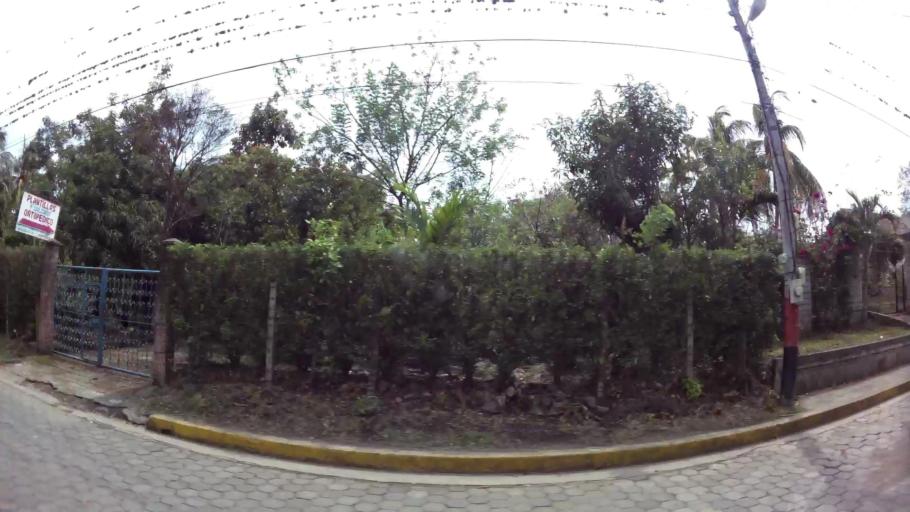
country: NI
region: Granada
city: Diriomo
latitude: 11.8791
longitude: -86.0529
